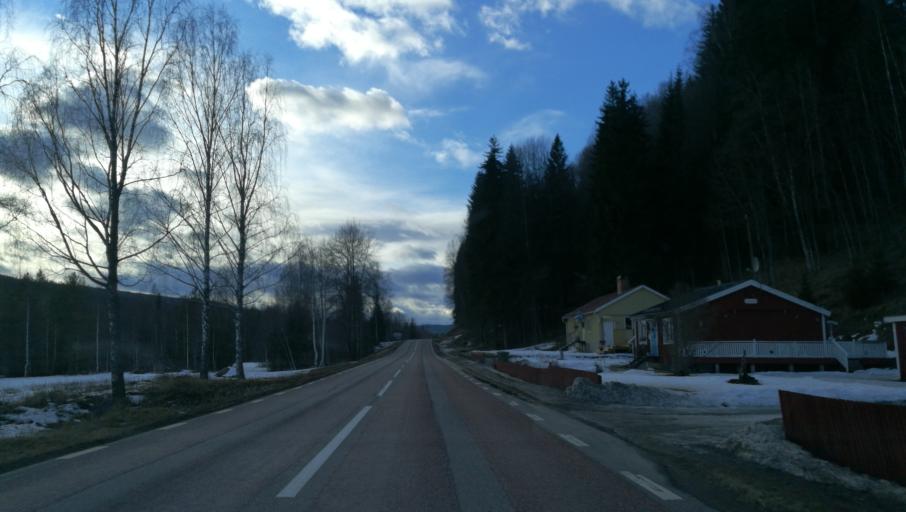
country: SE
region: Vaermland
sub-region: Torsby Kommun
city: Torsby
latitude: 60.7401
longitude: 12.8449
